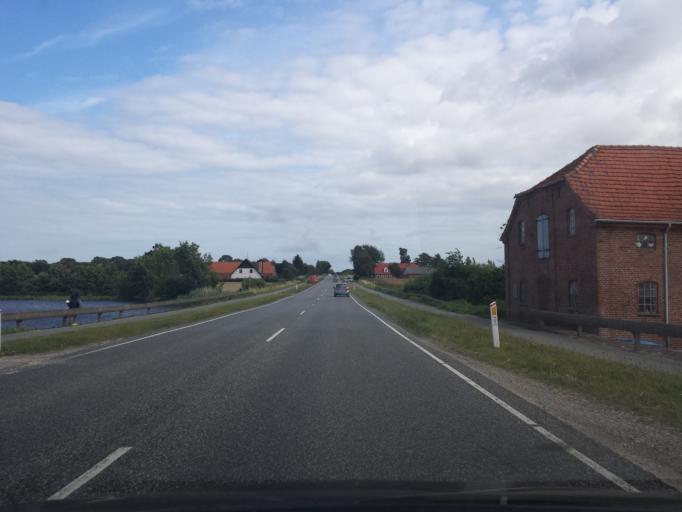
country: DK
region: South Denmark
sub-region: Sonderborg Kommune
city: Guderup
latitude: 54.9763
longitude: 9.8863
